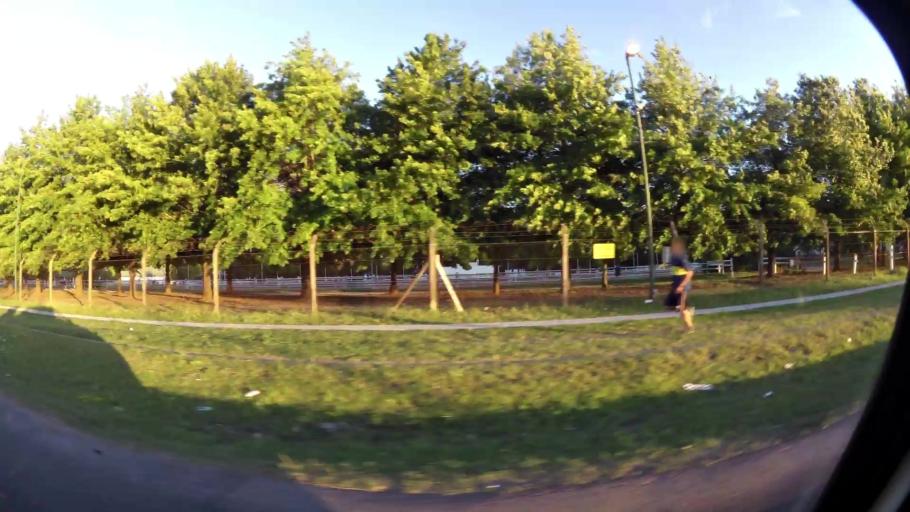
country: AR
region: Buenos Aires
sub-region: Partido de Quilmes
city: Quilmes
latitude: -34.8004
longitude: -58.1631
